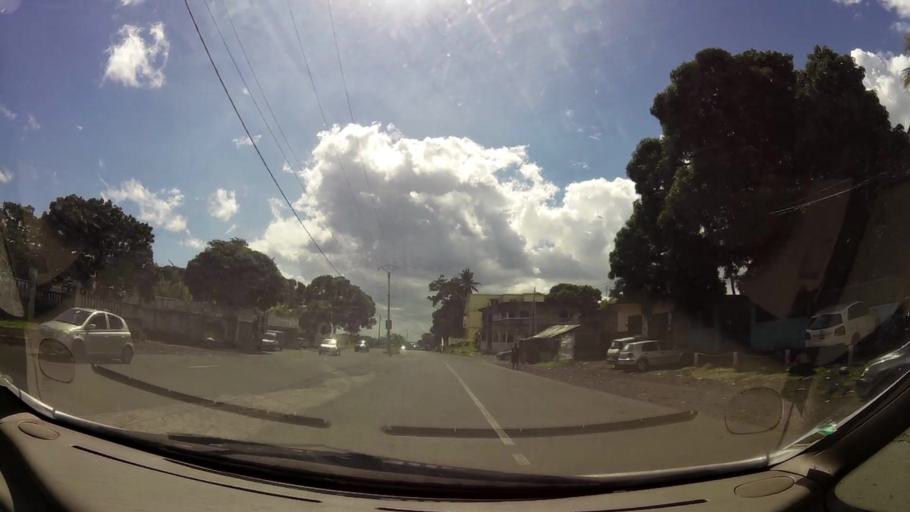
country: KM
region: Grande Comore
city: Mavingouni
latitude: -11.7134
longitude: 43.2461
